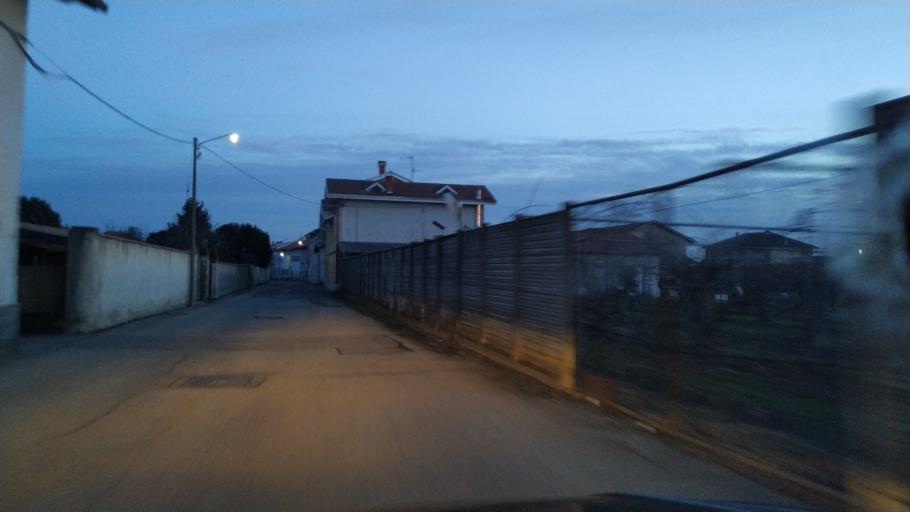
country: IT
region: Piedmont
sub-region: Provincia di Vercelli
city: Borgo d'Ale
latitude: 45.3502
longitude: 8.0466
